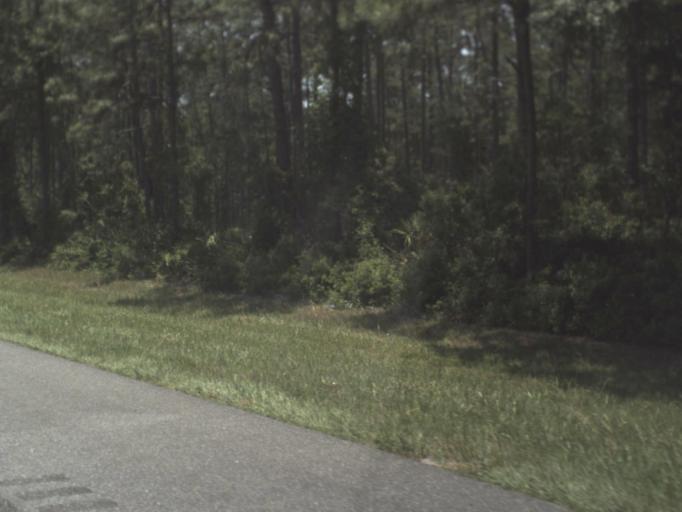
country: US
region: Florida
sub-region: Columbia County
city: Watertown
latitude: 30.2477
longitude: -82.5489
